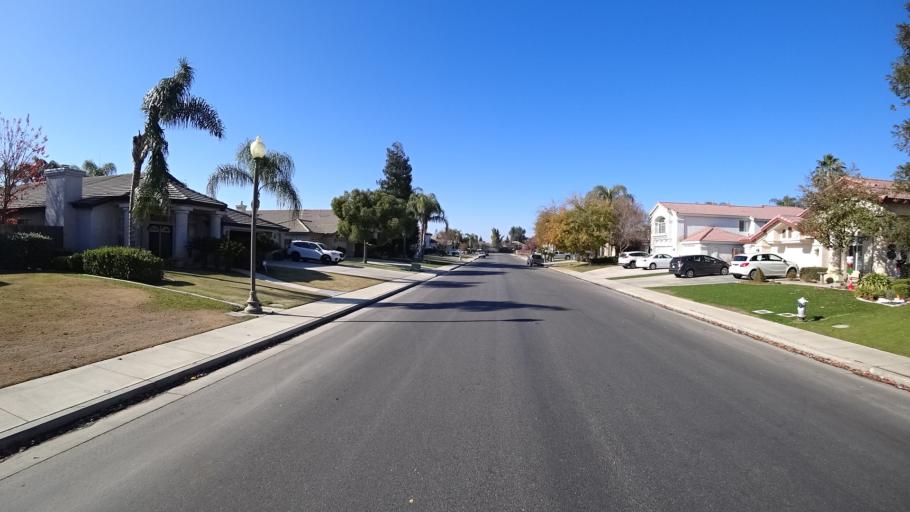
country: US
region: California
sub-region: Kern County
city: Rosedale
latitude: 35.3646
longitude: -119.1345
